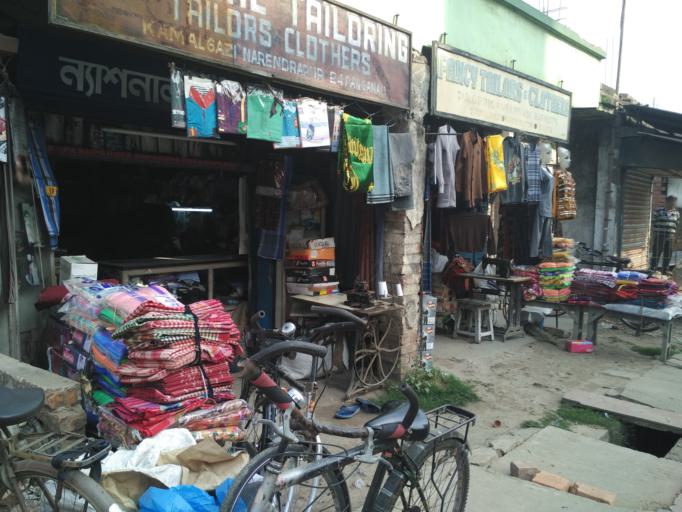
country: IN
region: West Bengal
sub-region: South 24 Paraganas
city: Baruipur
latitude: 22.4480
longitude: 88.3917
